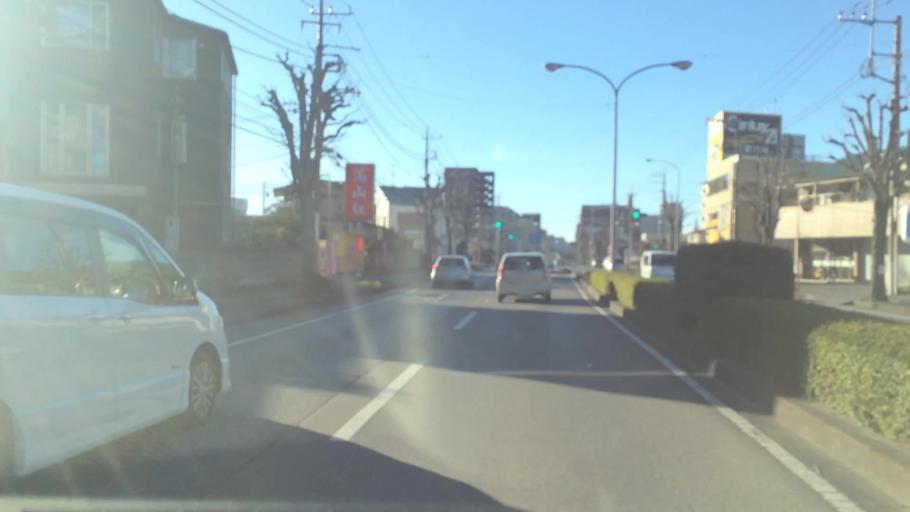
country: JP
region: Tochigi
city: Utsunomiya-shi
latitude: 36.5575
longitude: 139.9170
